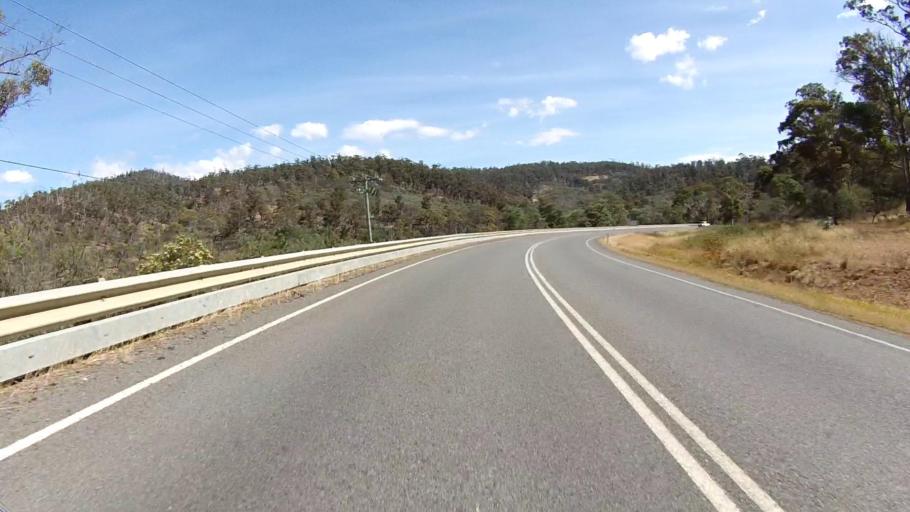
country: AU
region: Tasmania
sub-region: Sorell
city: Sorell
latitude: -42.6097
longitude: 147.6708
